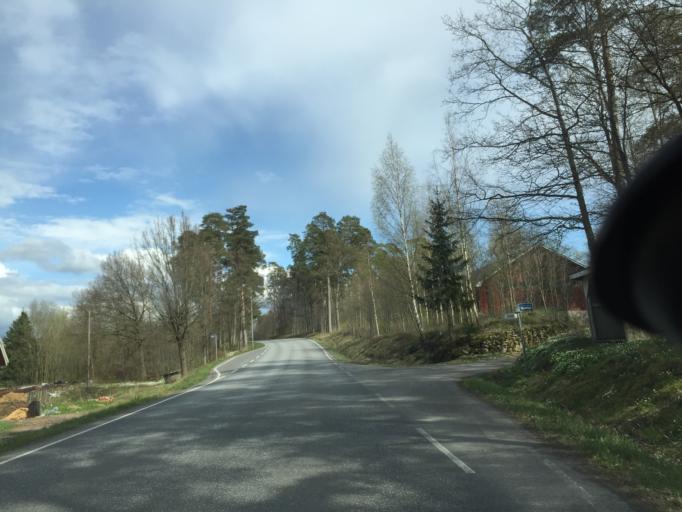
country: FI
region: Varsinais-Suomi
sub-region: Salo
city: Pernioe
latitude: 60.0336
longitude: 23.2141
